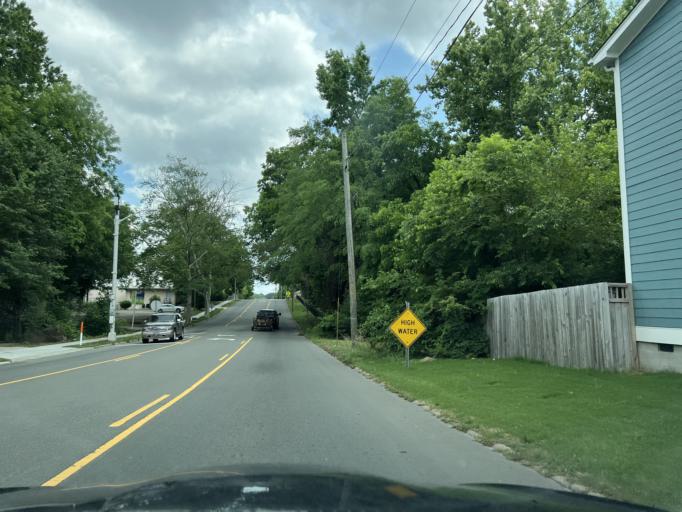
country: US
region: North Carolina
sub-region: Durham County
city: Durham
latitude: 35.9987
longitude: -78.8860
